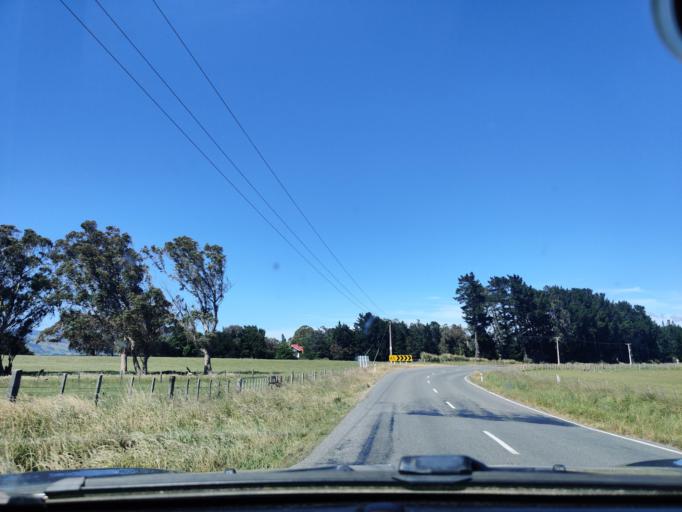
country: NZ
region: Wellington
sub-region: South Wairarapa District
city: Waipawa
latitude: -41.2243
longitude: 175.3524
